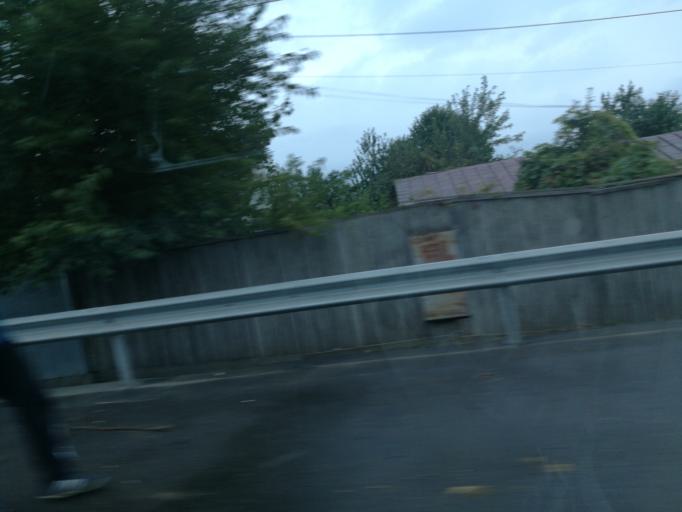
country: RO
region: Galati
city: Galati
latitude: 45.4669
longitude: 28.0349
